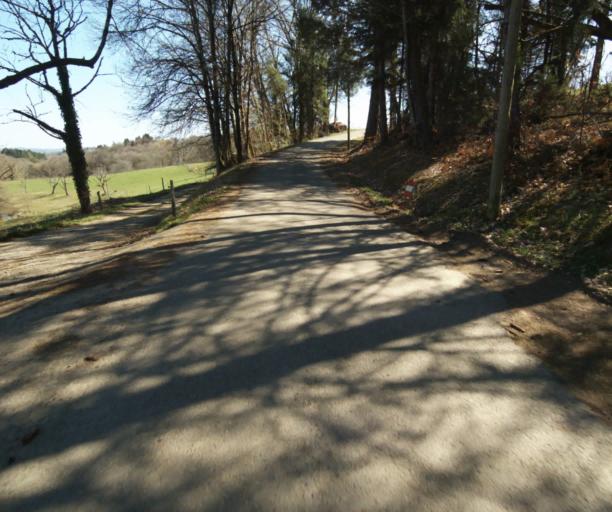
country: FR
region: Limousin
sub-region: Departement de la Correze
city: Chameyrat
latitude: 45.2807
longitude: 1.7056
